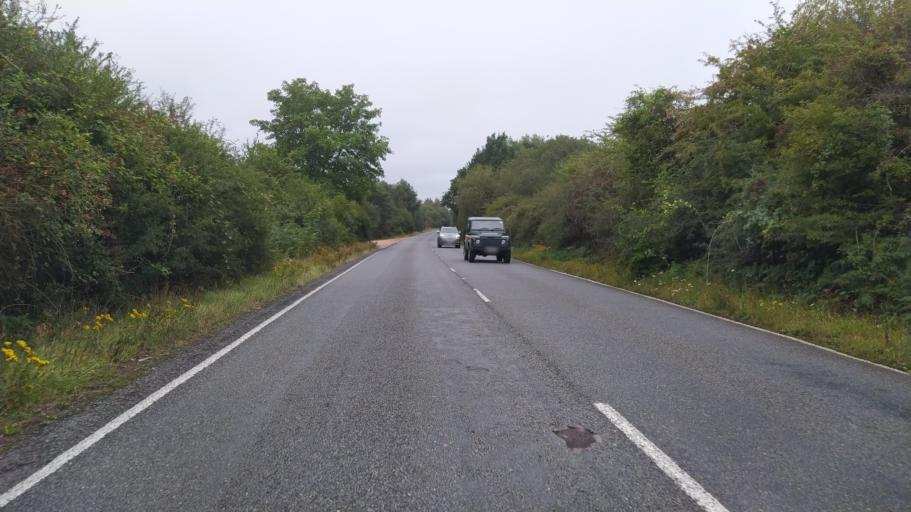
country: GB
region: England
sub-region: Hampshire
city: Sway
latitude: 50.8278
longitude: -1.6498
